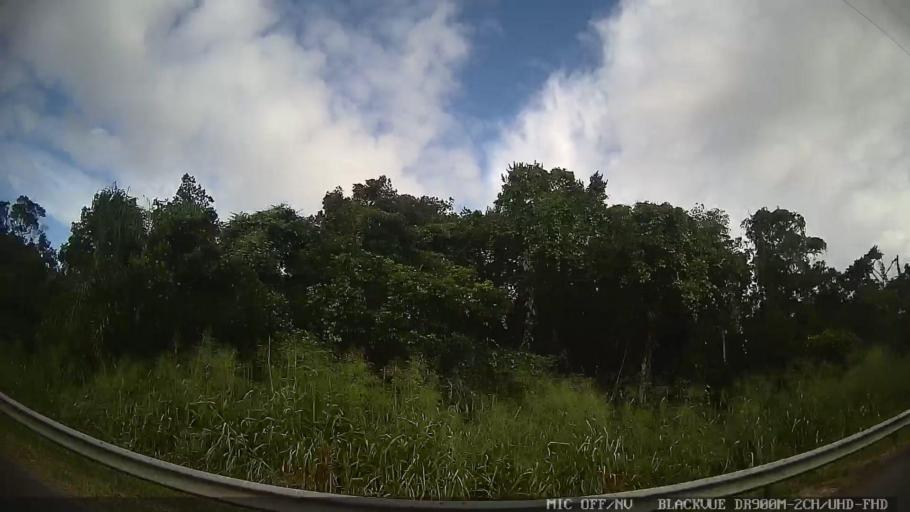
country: BR
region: Sao Paulo
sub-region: Peruibe
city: Peruibe
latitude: -24.2515
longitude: -46.9303
